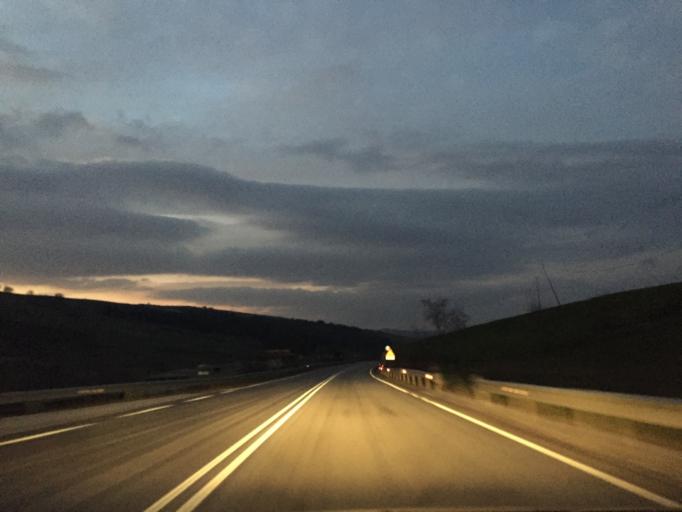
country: IT
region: Apulia
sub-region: Provincia di Foggia
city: Volturara Appula
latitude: 41.4594
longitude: 15.0607
